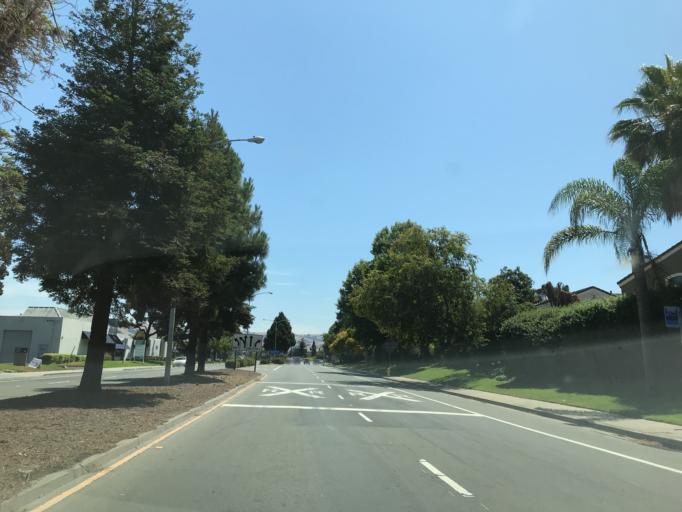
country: US
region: California
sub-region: Alameda County
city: Union City
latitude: 37.6057
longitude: -122.0718
